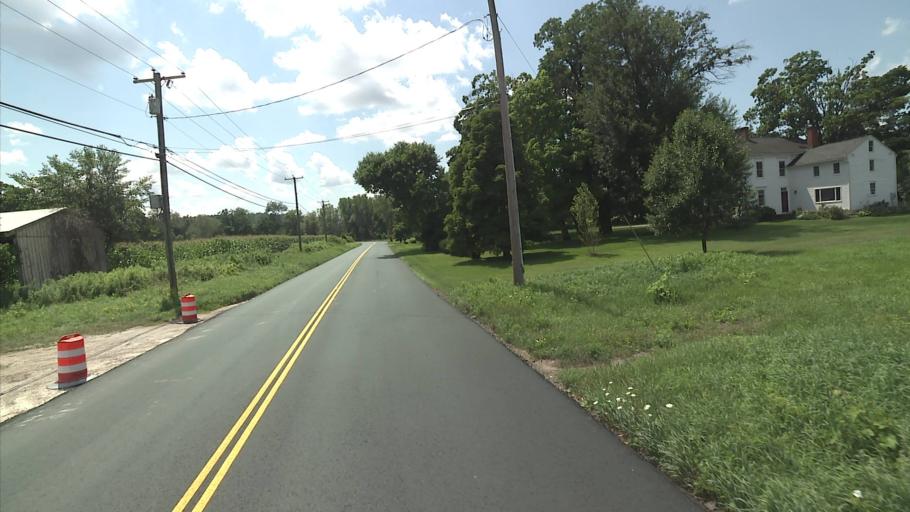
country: US
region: Connecticut
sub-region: Litchfield County
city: Canaan
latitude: 41.9735
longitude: -73.3577
